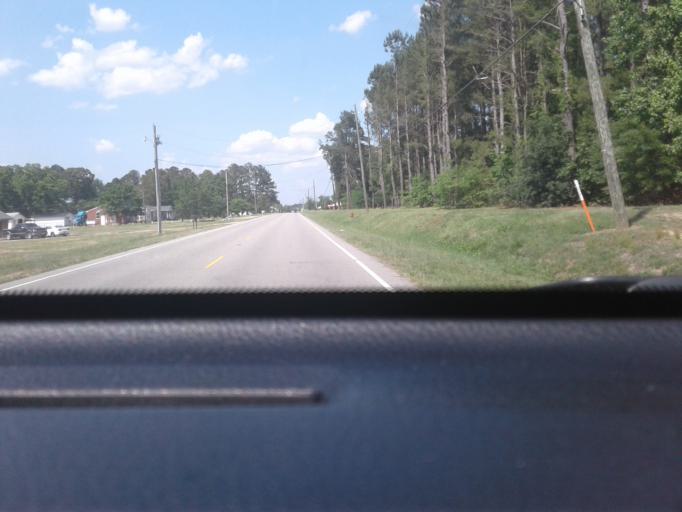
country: US
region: North Carolina
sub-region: Cumberland County
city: Eastover
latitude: 35.1570
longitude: -78.7325
